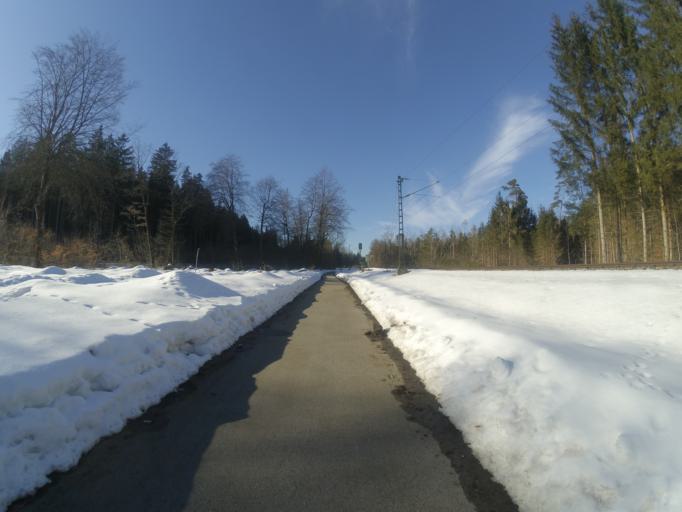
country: DE
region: Bavaria
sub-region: Upper Bavaria
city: Hohenkirchen-Siegertsbrunn
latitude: 48.0000
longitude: 11.7312
